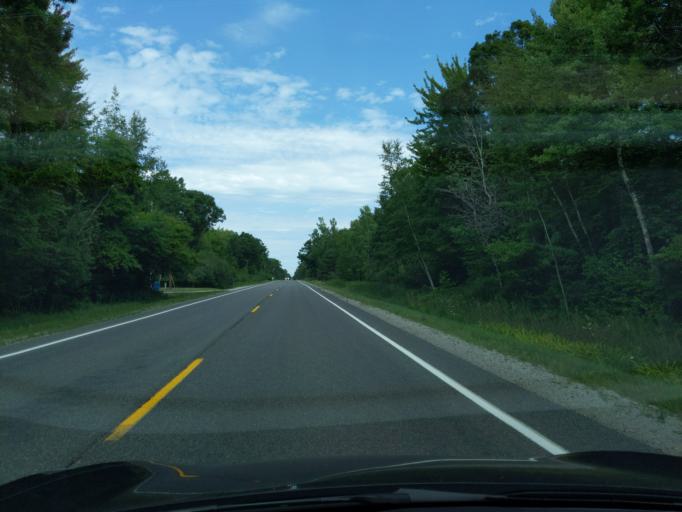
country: US
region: Michigan
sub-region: Midland County
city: Midland
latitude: 43.5308
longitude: -84.3698
